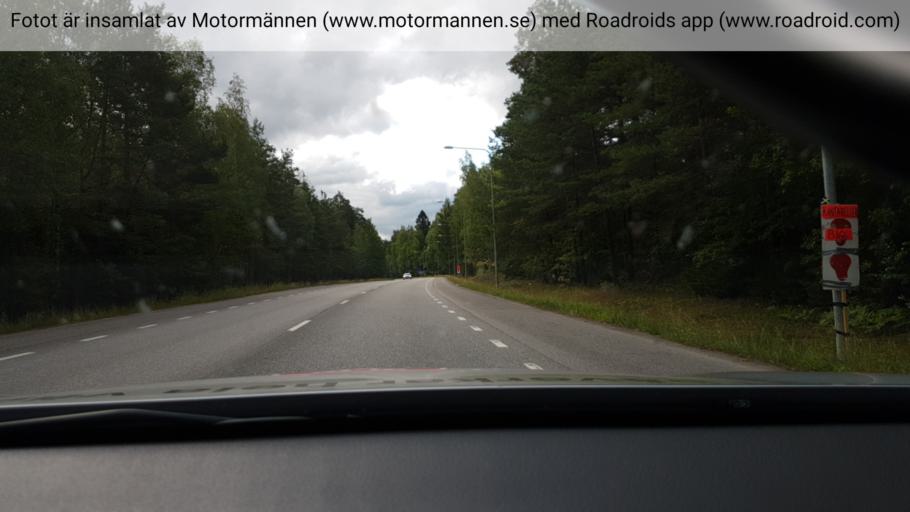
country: SE
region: Stockholm
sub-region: Nacka Kommun
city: Alta
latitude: 59.2372
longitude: 18.1891
